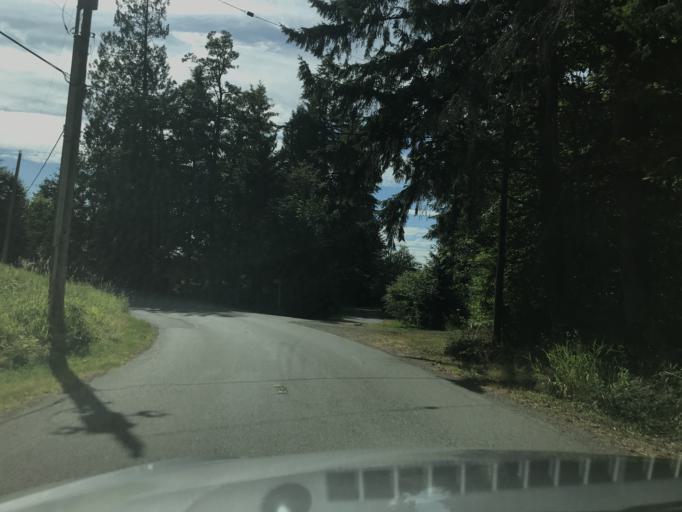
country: US
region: Washington
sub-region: King County
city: Hobart
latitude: 47.4159
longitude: -121.9380
